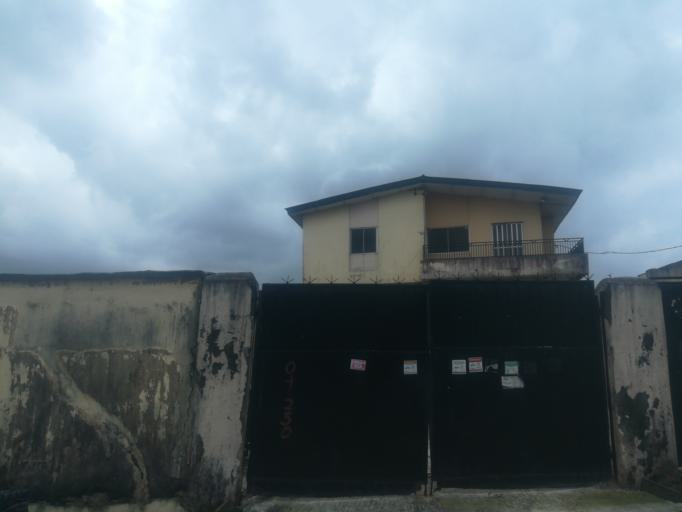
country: NG
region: Lagos
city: Ojota
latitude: 6.5646
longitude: 3.3901
